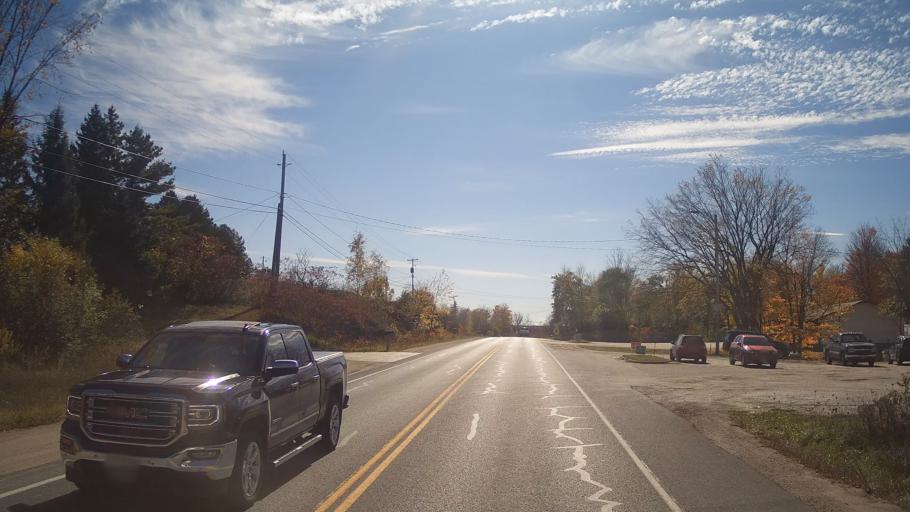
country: CA
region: Ontario
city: Perth
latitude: 44.7881
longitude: -76.6781
